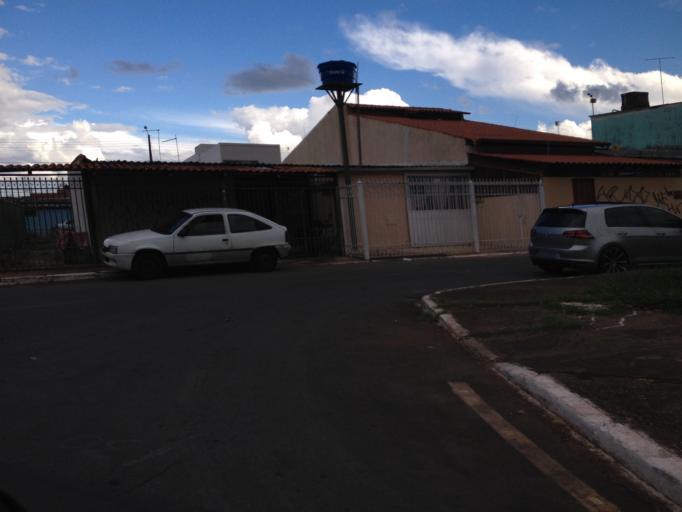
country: BR
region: Federal District
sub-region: Brasilia
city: Brasilia
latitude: -15.7883
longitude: -47.9376
